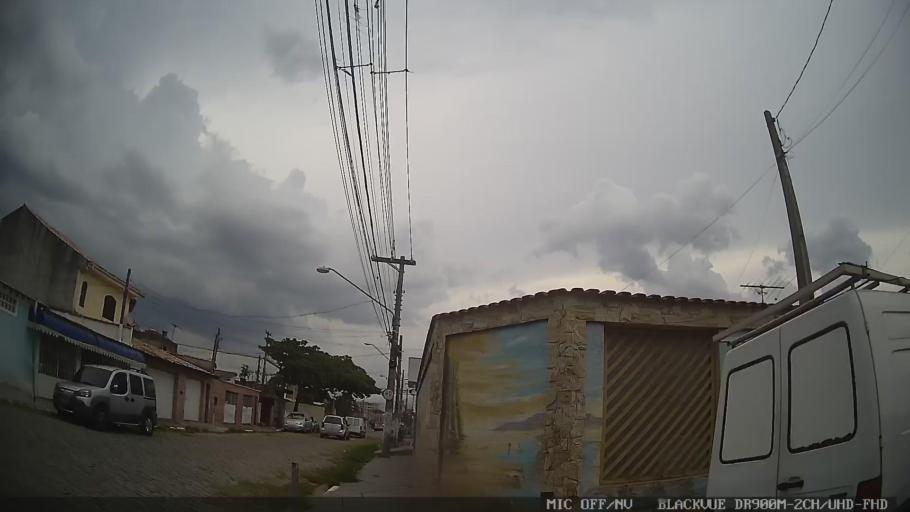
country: BR
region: Sao Paulo
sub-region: Suzano
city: Suzano
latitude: -23.5446
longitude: -46.2943
